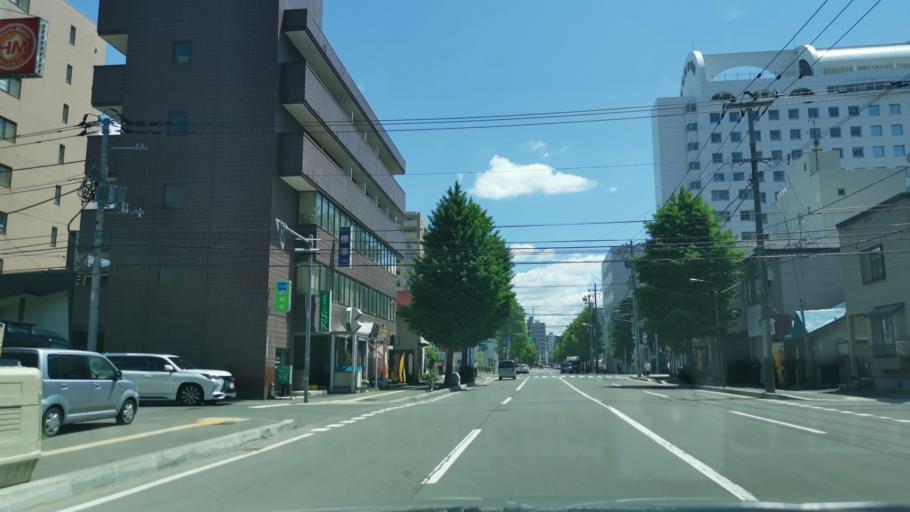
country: JP
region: Hokkaido
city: Sapporo
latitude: 43.0577
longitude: 141.3364
